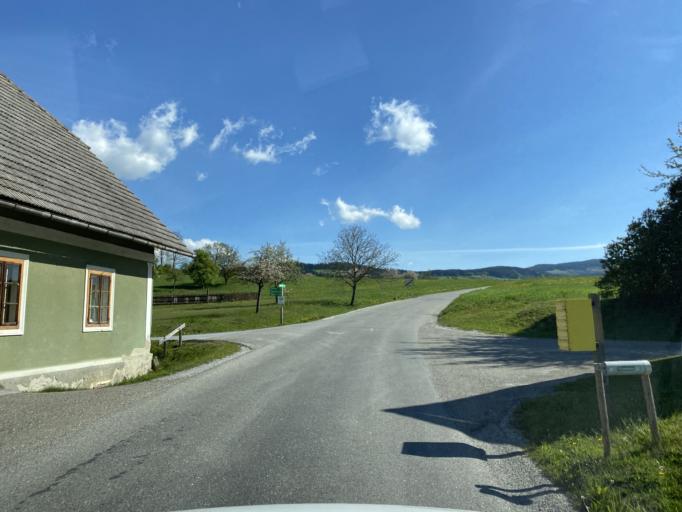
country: AT
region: Styria
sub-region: Politischer Bezirk Weiz
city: Strallegg
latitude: 47.3691
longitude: 15.7129
